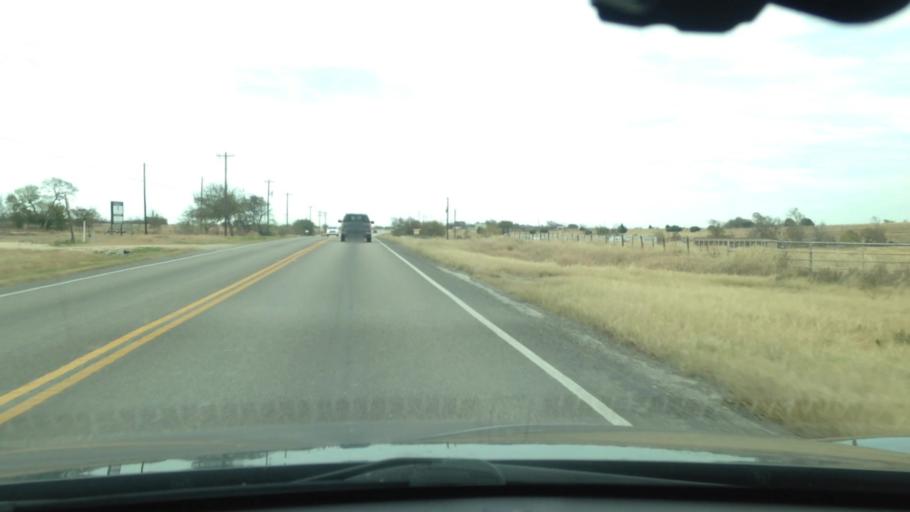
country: US
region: Texas
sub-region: Caldwell County
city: Martindale
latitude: 29.9127
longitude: -97.8539
